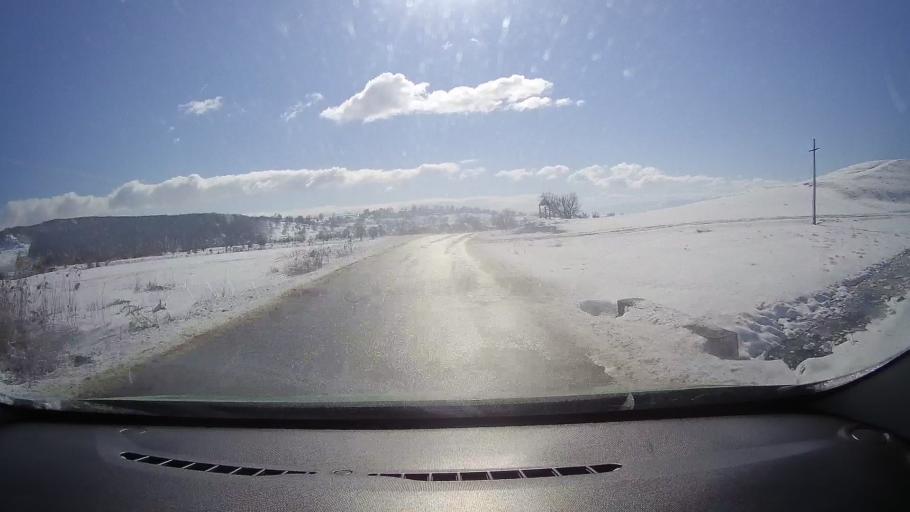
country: RO
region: Sibiu
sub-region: Comuna Vurpar
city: Vurpar
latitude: 45.8652
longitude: 24.3189
